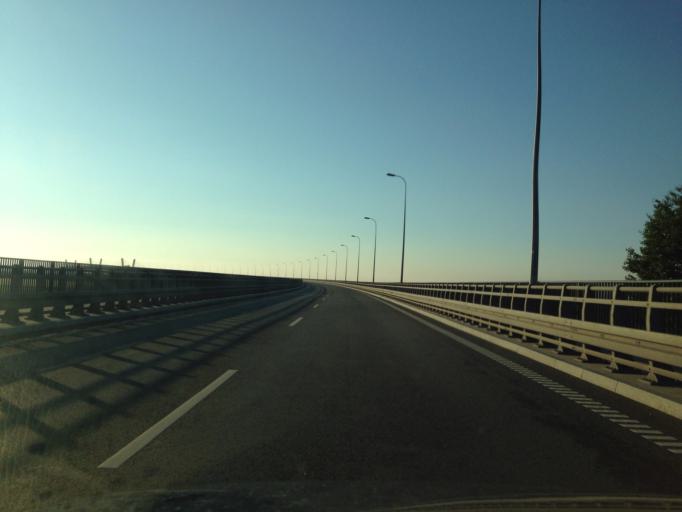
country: PL
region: Pomeranian Voivodeship
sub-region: Powiat tczewski
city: Gniew
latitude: 53.7590
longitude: 18.8273
